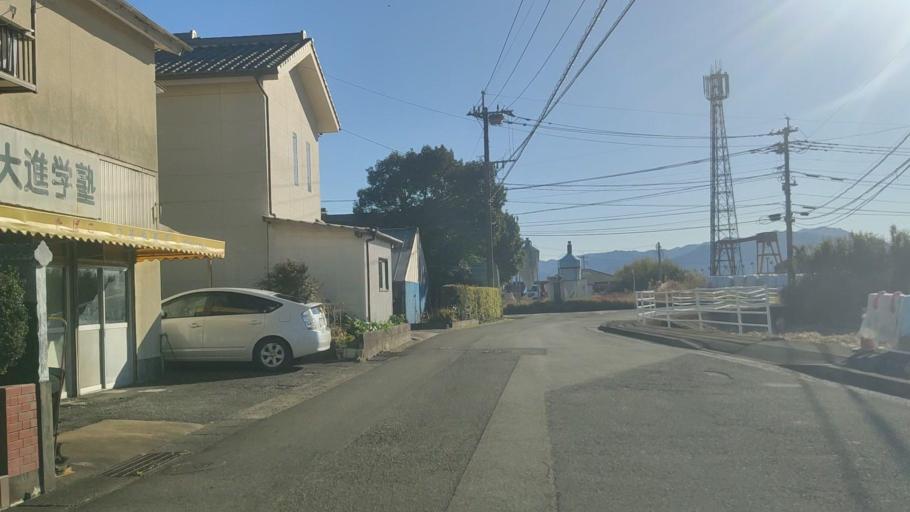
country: JP
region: Miyazaki
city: Miyazaki-shi
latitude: 31.8685
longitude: 131.4434
